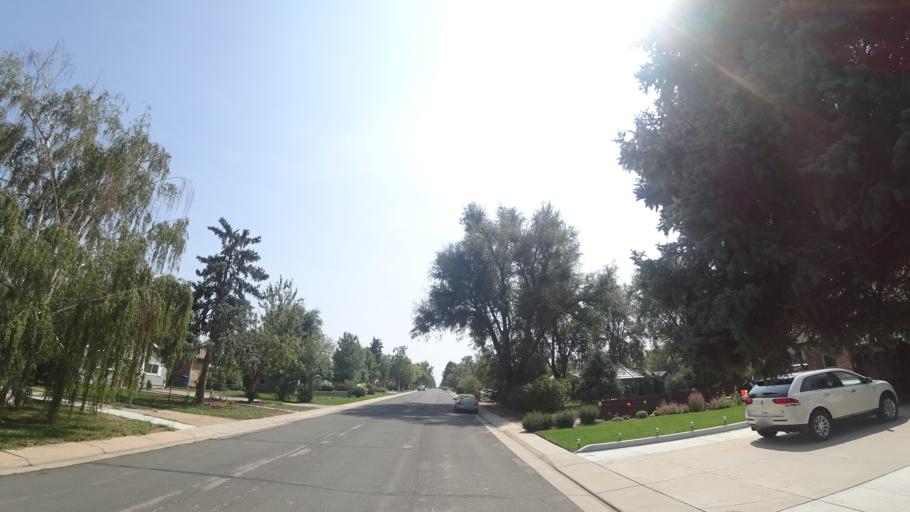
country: US
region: Colorado
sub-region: Arapahoe County
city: Englewood
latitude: 39.6311
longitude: -104.9961
